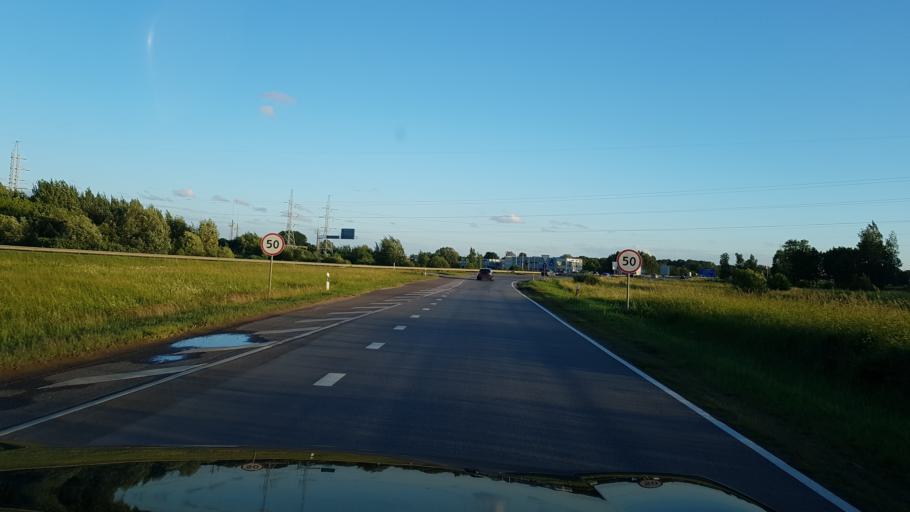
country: LT
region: Kauno apskritis
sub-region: Kaunas
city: Sargenai
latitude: 54.9397
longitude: 23.8762
